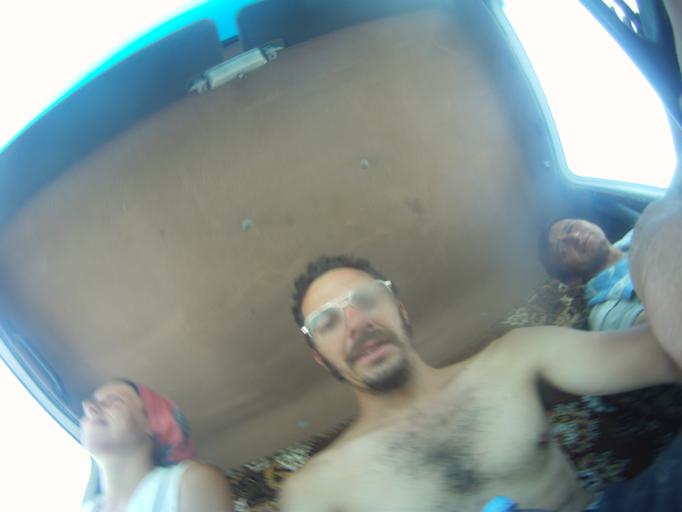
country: KZ
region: Ongtustik Qazaqstan
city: Shayan
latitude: 42.9689
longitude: 68.8735
